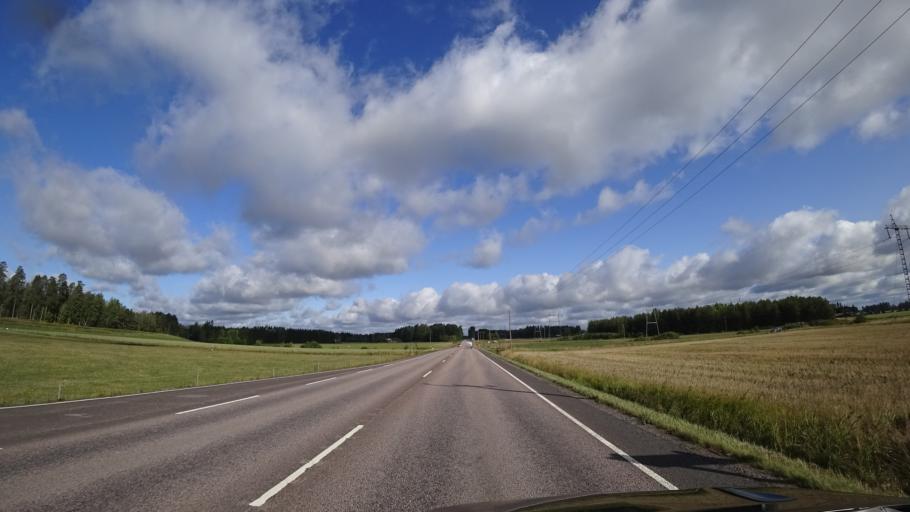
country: FI
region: Uusimaa
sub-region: Helsinki
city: Hyvinge
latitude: 60.5187
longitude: 24.9261
